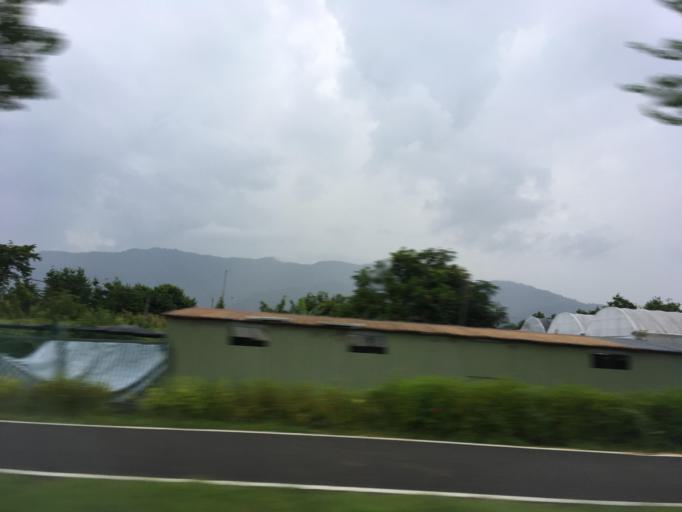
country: TW
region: Taiwan
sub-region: Yilan
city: Yilan
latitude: 24.6772
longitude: 121.6416
